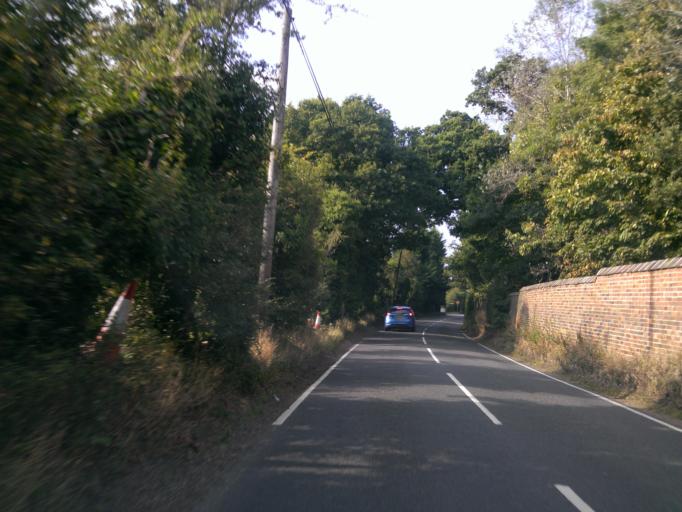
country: GB
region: England
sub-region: Essex
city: Great Totham
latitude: 51.8062
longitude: 0.6804
